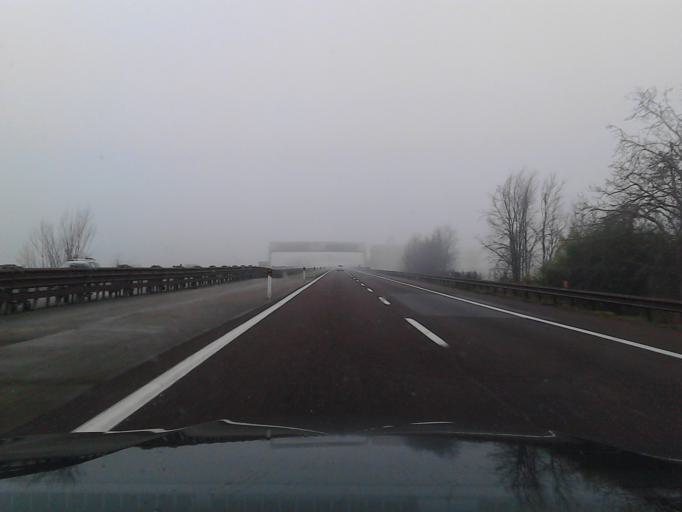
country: IT
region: Emilia-Romagna
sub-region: Provincia di Modena
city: Santa Croce Scuole
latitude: 44.7399
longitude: 10.8445
